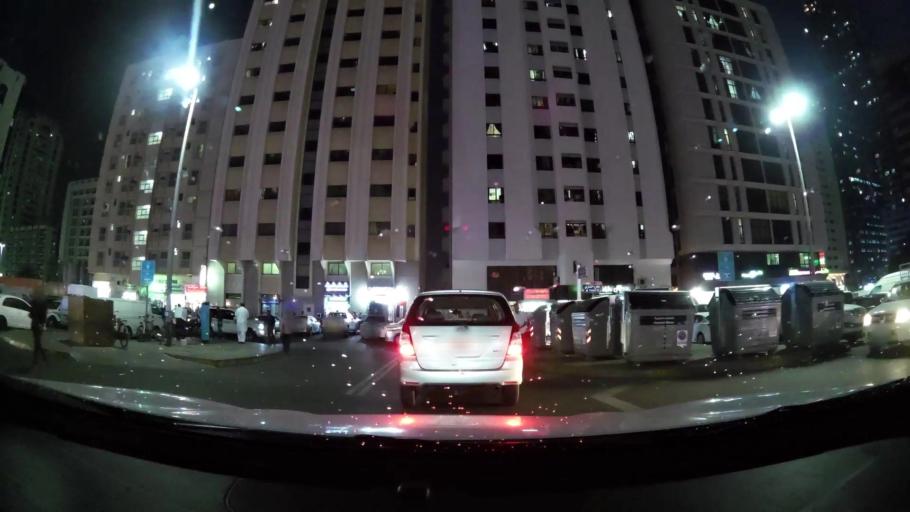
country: AE
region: Abu Dhabi
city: Abu Dhabi
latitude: 24.4859
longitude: 54.3616
